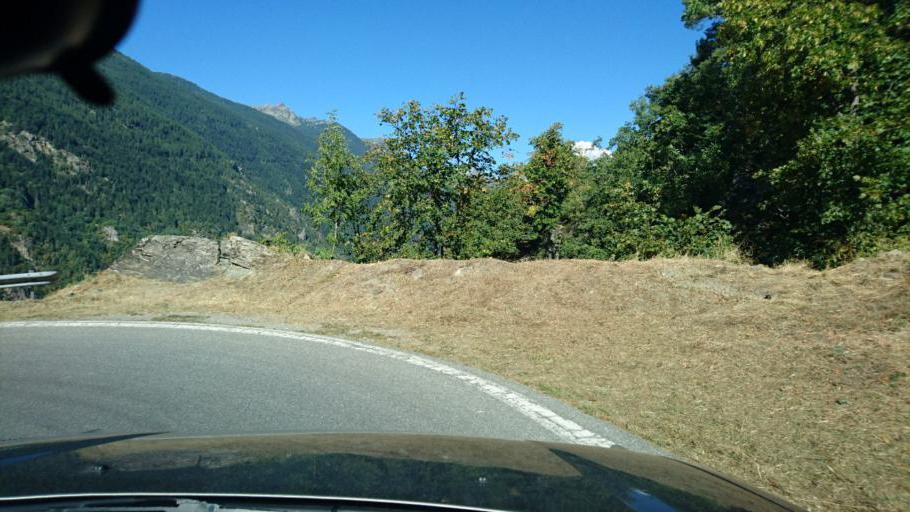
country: IT
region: Aosta Valley
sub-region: Valle d'Aosta
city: Avise
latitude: 45.7137
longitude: 7.1238
